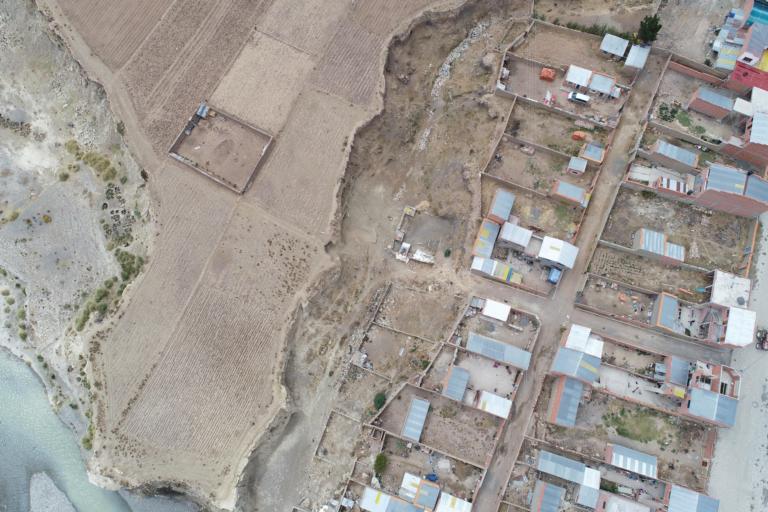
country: BO
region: La Paz
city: Achacachi
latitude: -16.0396
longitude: -68.6831
